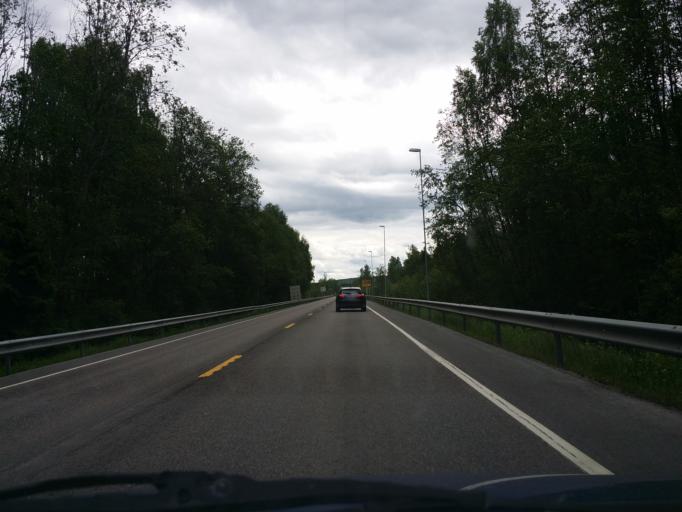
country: NO
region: Hedmark
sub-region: Hamar
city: Hamar
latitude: 60.8098
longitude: 11.1049
